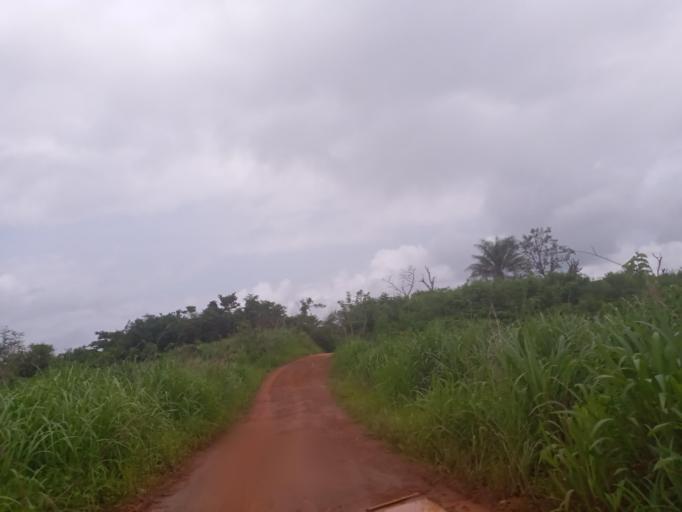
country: SL
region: Northern Province
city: Bumbuna
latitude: 8.9638
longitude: -11.7567
